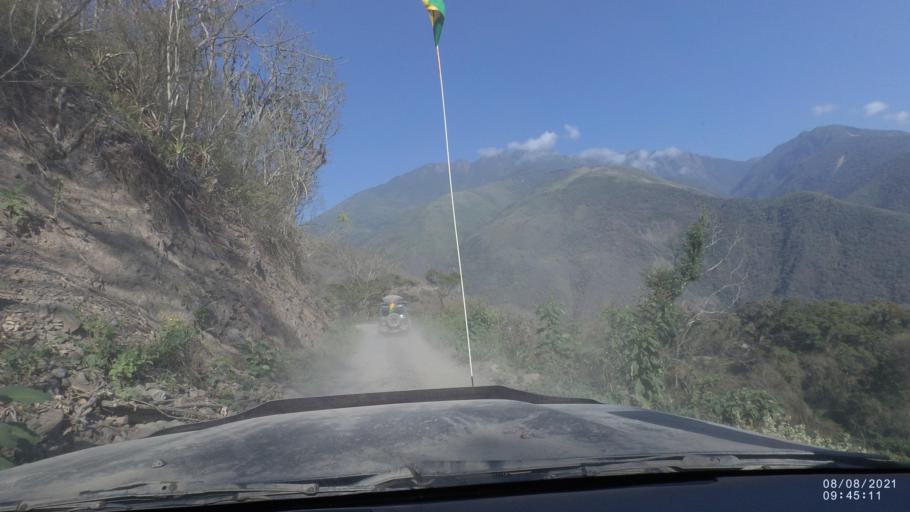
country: BO
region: La Paz
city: Quime
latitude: -16.6031
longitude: -66.7257
